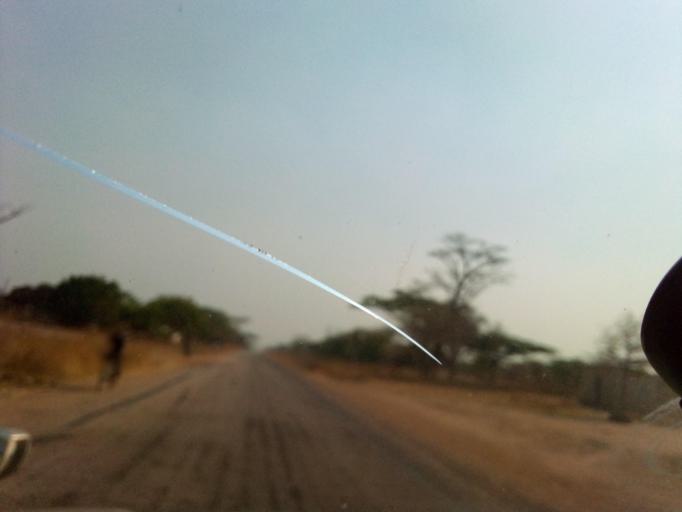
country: ZM
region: Northern
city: Chinsali
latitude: -10.9371
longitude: 32.0408
